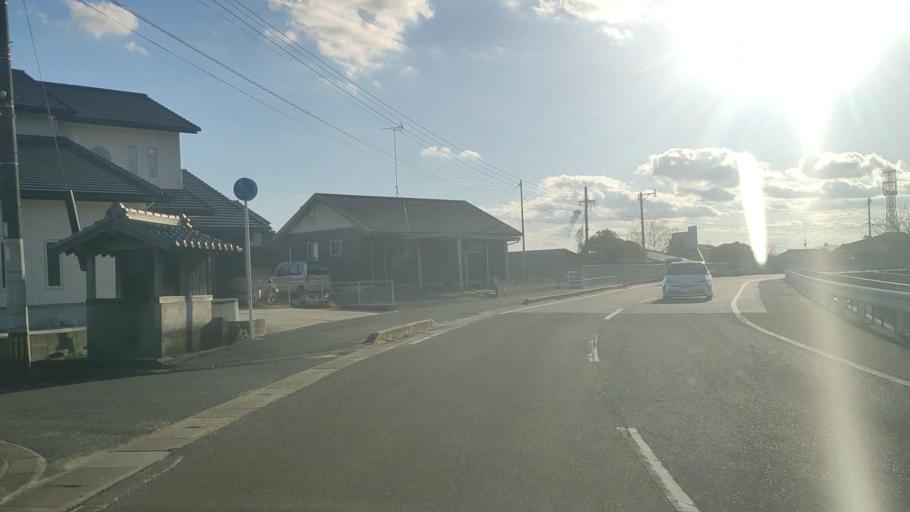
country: JP
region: Saga Prefecture
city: Saga-shi
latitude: 33.3059
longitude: 130.2585
